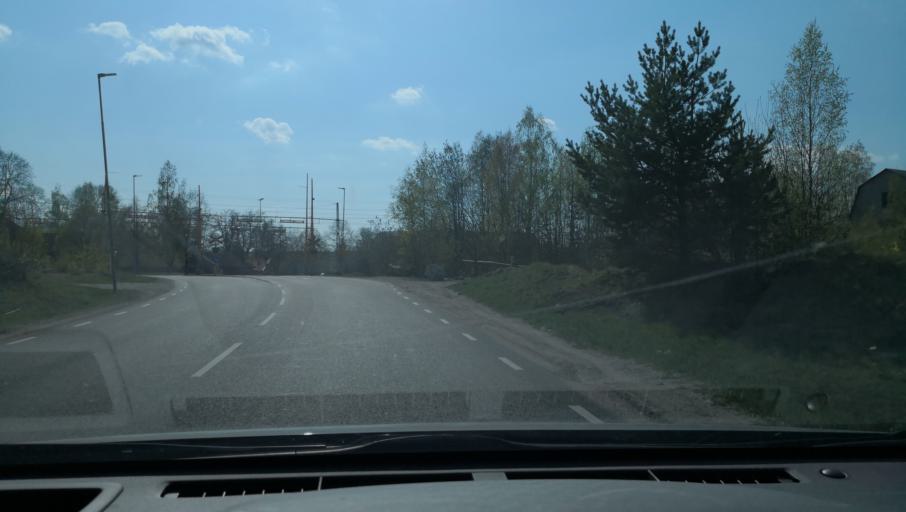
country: SE
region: Vaestmanland
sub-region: Sala Kommun
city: Sala
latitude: 59.9293
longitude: 16.5956
